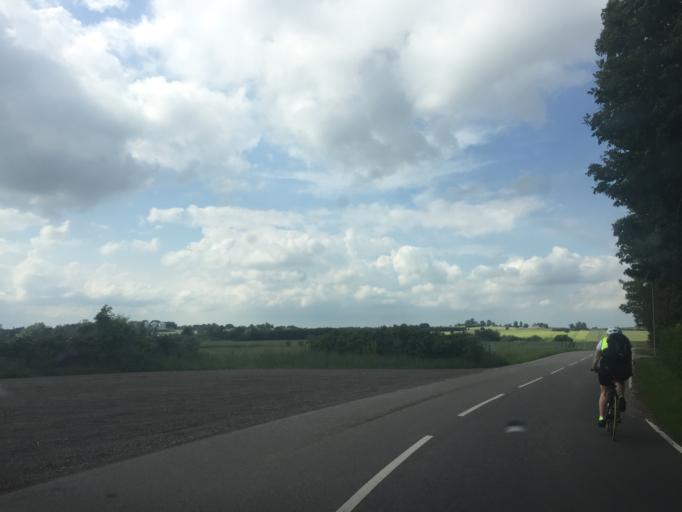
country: DK
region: Capital Region
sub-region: Hoje-Taastrup Kommune
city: Flong
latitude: 55.6785
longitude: 12.1874
